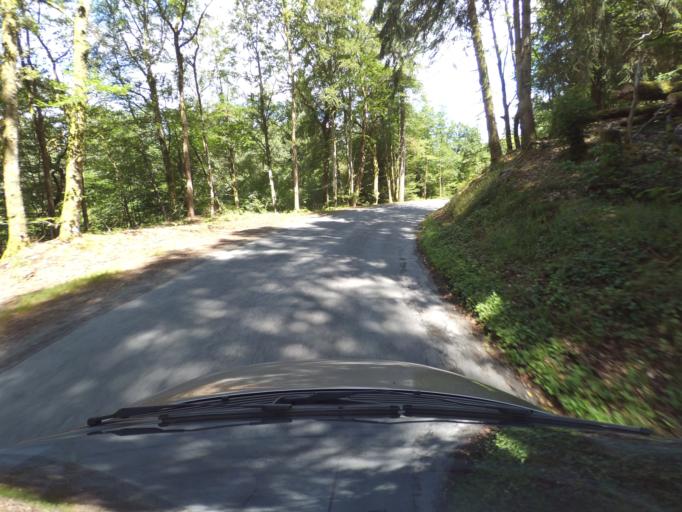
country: FR
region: Limousin
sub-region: Departement de la Creuse
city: Banize
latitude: 45.7948
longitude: 1.9336
